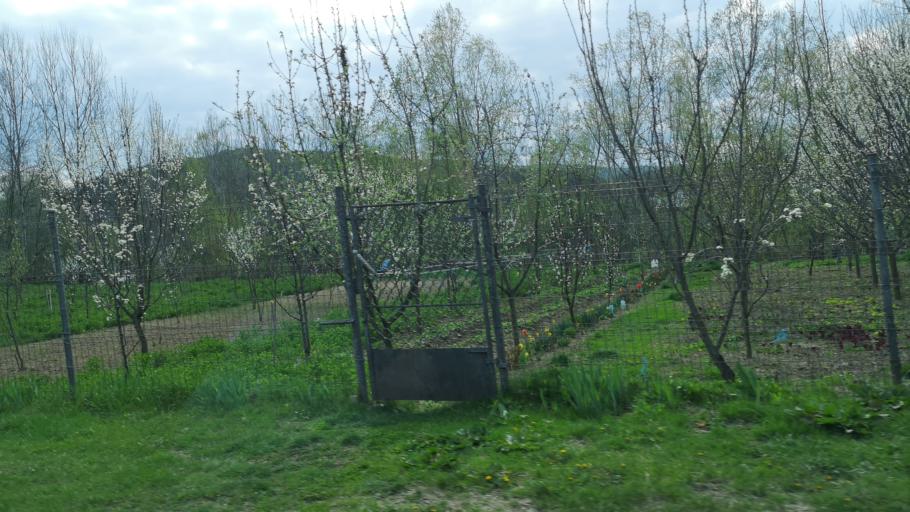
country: RO
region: Prahova
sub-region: Comuna Soimari
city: Soimari
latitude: 45.1750
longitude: 26.2123
